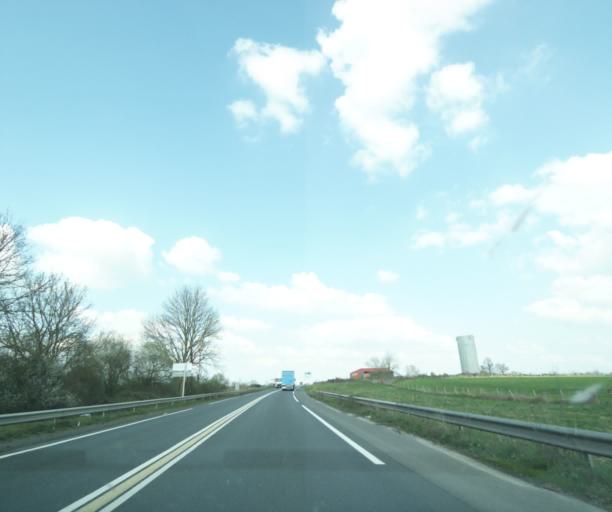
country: FR
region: Auvergne
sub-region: Departement de l'Allier
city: Montmarault
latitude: 46.3277
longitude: 2.9696
